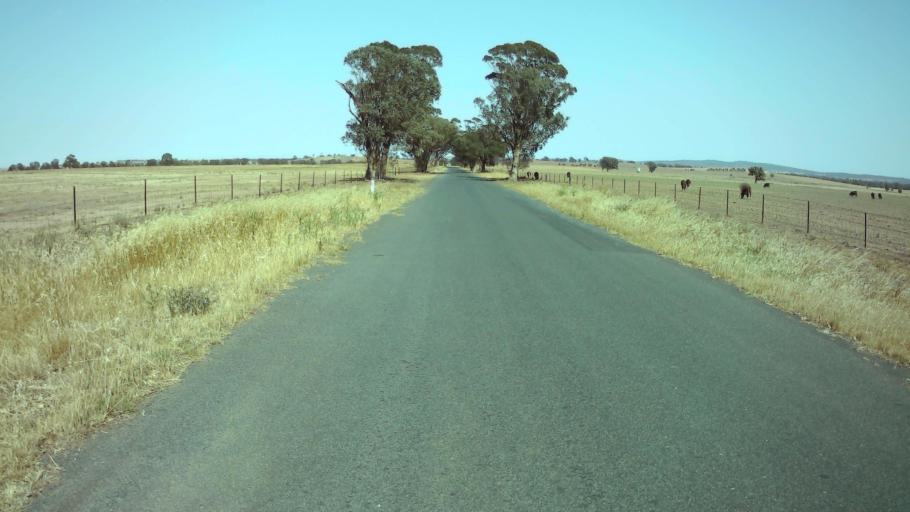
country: AU
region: New South Wales
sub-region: Weddin
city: Grenfell
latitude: -33.8590
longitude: 147.9698
